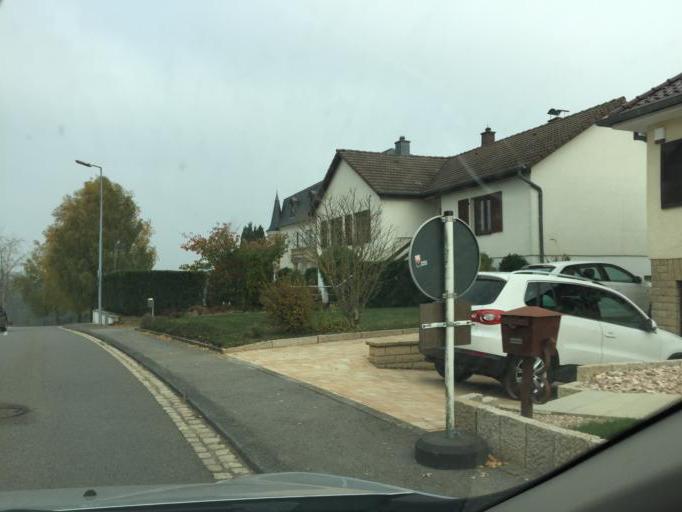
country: LU
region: Luxembourg
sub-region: Canton de Luxembourg
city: Sandweiler
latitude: 49.6185
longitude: 6.2142
